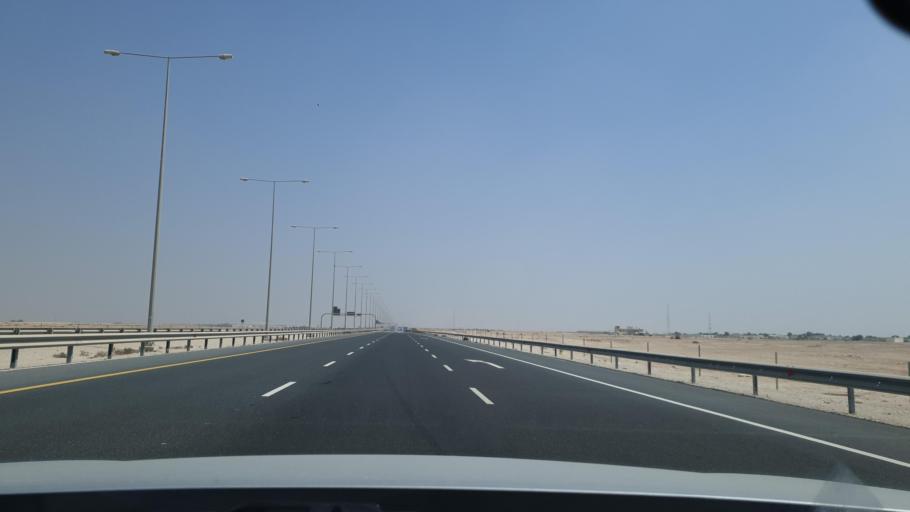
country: QA
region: Baladiyat az Za`ayin
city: Az Za`ayin
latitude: 25.6185
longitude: 51.3809
